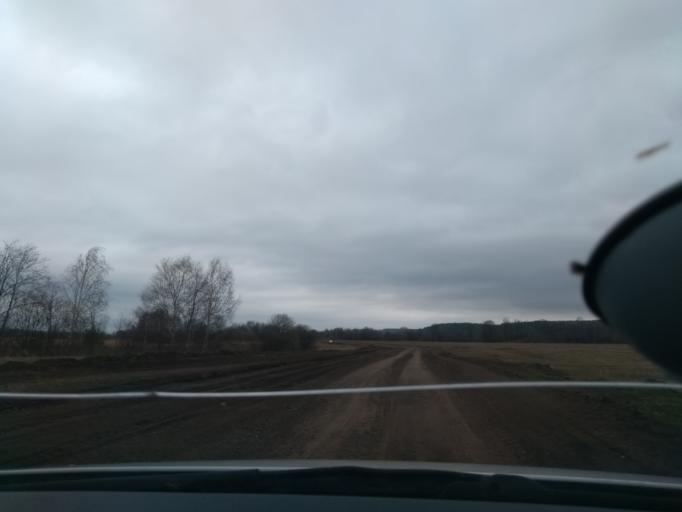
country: RU
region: Perm
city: Orda
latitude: 57.2328
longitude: 56.6090
